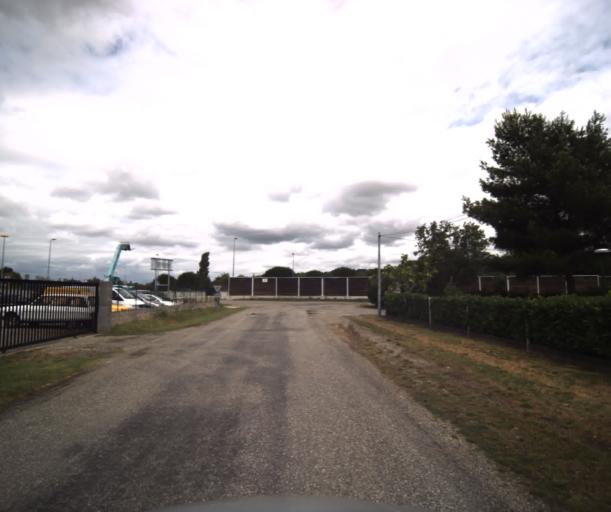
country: FR
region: Midi-Pyrenees
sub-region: Departement de la Haute-Garonne
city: Lacroix-Falgarde
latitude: 43.4827
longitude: 1.4012
